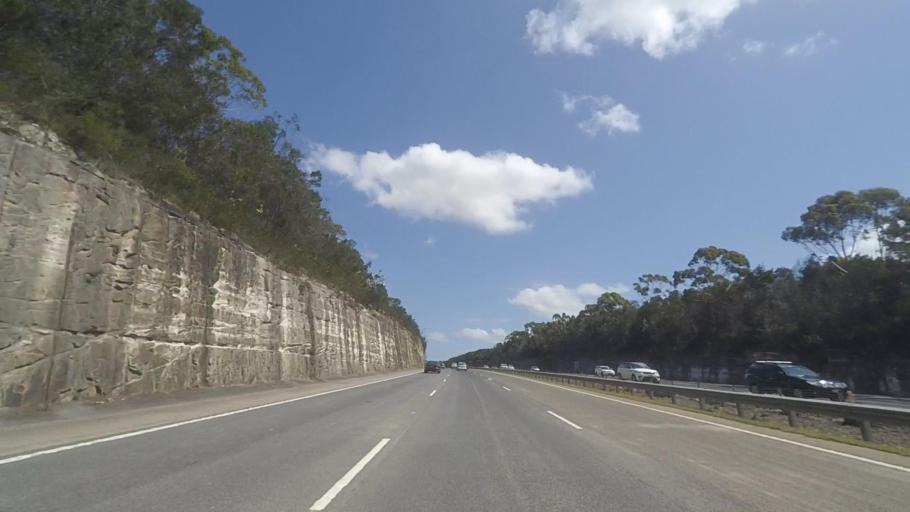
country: AU
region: New South Wales
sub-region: Hornsby Shire
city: Mount Colah
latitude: -33.6743
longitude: 151.1201
